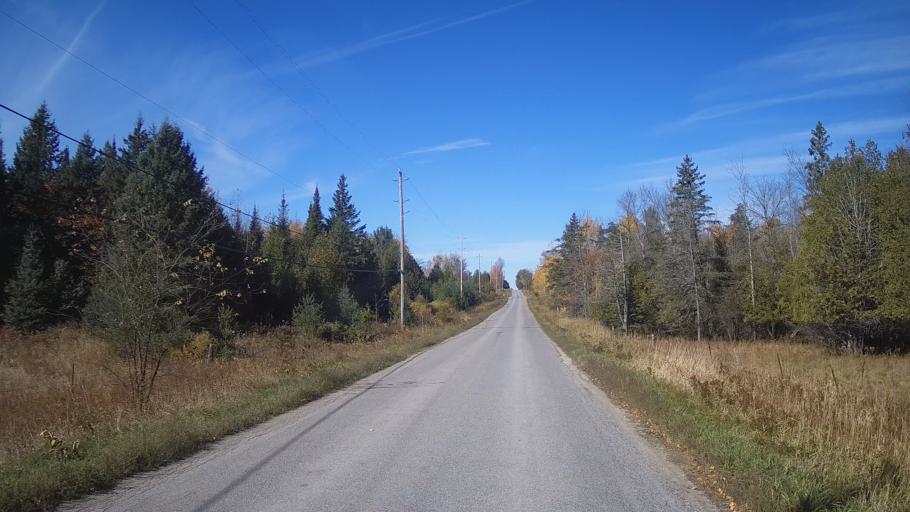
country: CA
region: Ontario
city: Perth
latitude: 44.8492
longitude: -76.3703
